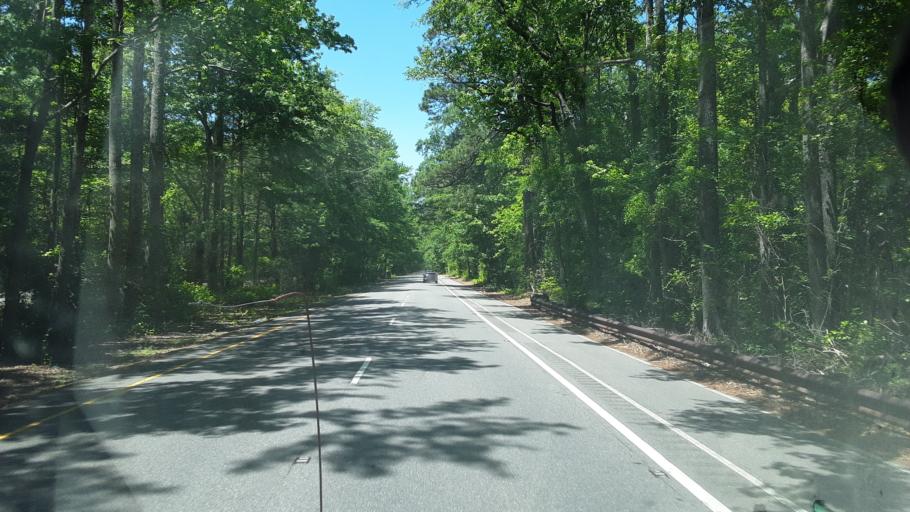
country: US
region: Virginia
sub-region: City of Virginia Beach
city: Virginia Beach
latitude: 36.9106
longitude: -76.0042
